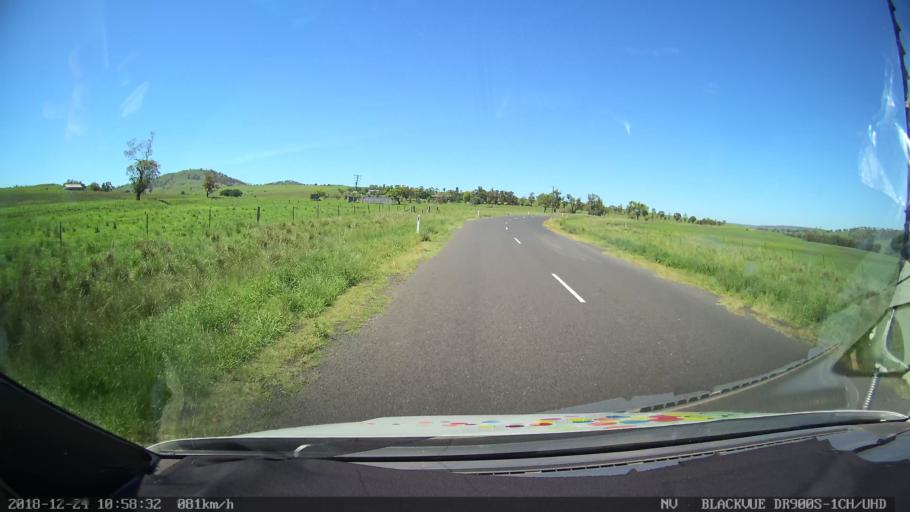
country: AU
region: New South Wales
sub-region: Upper Hunter Shire
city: Merriwa
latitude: -32.0487
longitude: 150.4060
